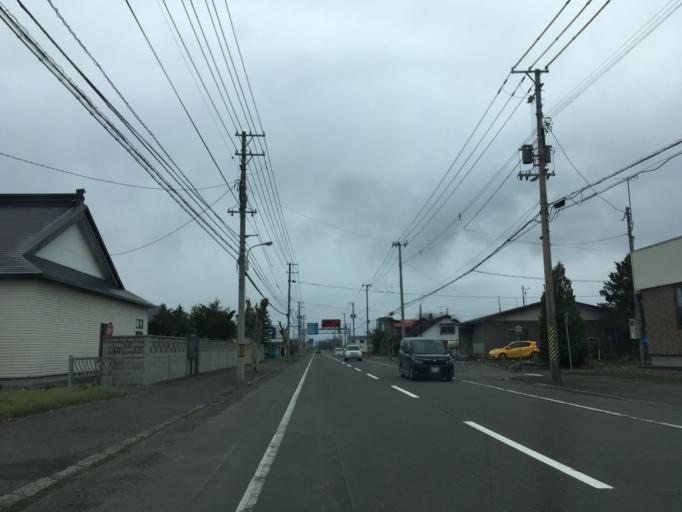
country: JP
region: Hokkaido
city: Chitose
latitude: 42.9460
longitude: 141.8035
